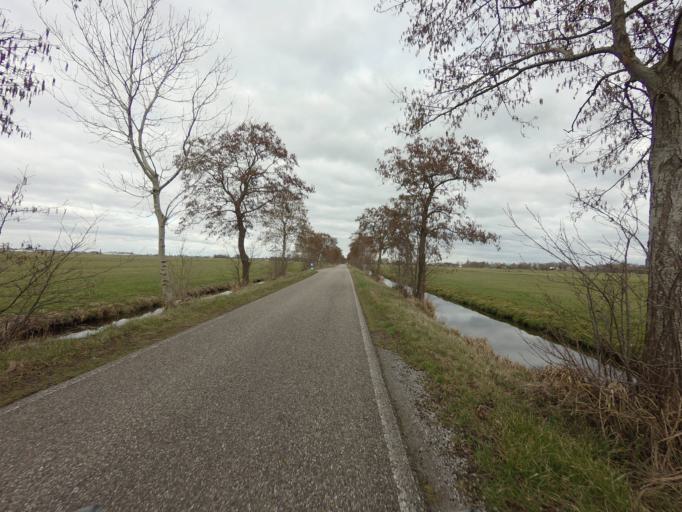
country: NL
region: South Holland
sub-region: Gemeente Alphen aan den Rijn
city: Alphen aan den Rijn
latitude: 52.1494
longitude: 4.7126
